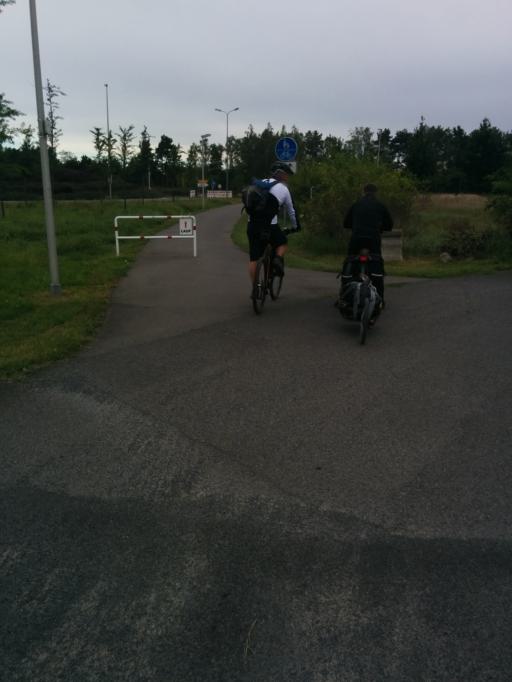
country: DE
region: Brandenburg
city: Cottbus
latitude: 51.7700
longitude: 14.3131
